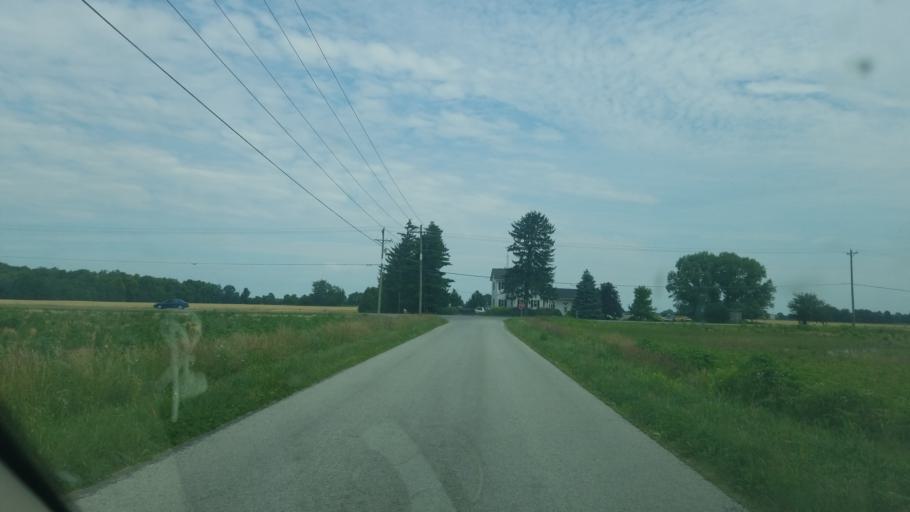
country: US
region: Ohio
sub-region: Seneca County
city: Fostoria
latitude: 41.0720
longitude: -83.4634
